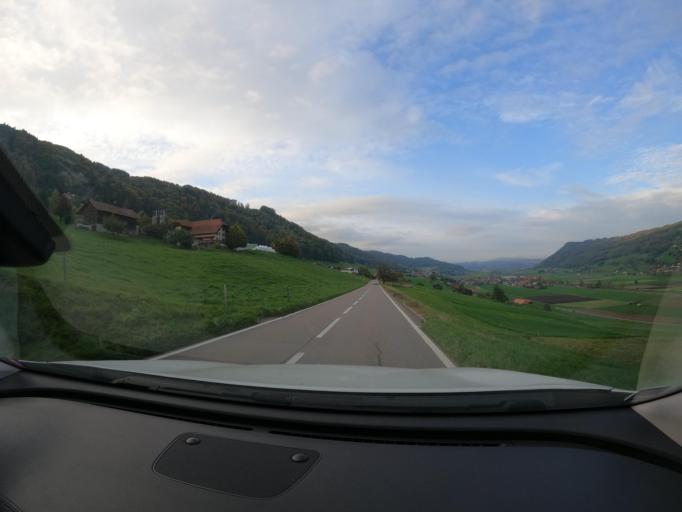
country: CH
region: Bern
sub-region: Bern-Mittelland District
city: Toffen
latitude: 46.8454
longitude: 7.4919
